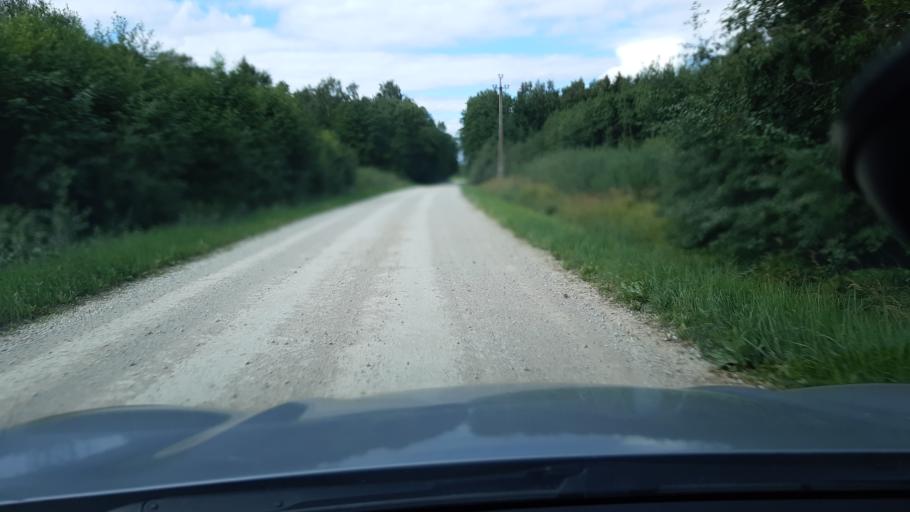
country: EE
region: Raplamaa
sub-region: Jaervakandi vald
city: Jarvakandi
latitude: 58.7949
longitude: 24.9722
